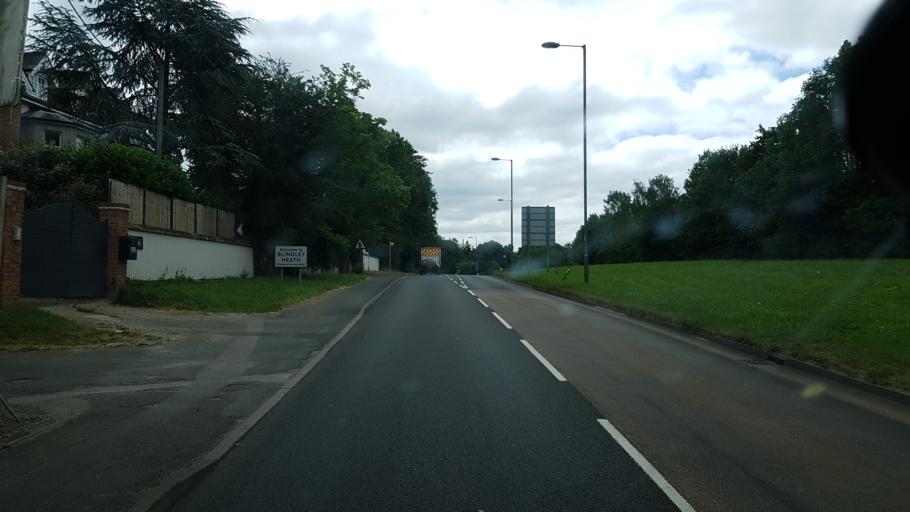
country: GB
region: England
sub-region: Surrey
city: Godstone
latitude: 51.2035
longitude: -0.0568
